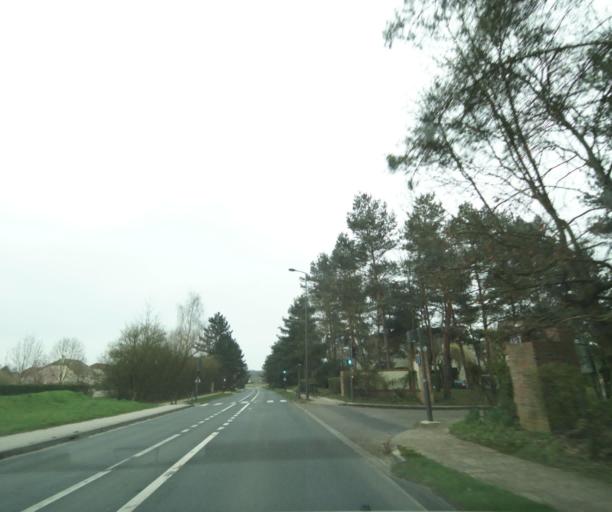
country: FR
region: Ile-de-France
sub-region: Departement du Val-d'Oise
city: Courdimanche
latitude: 49.0417
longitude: 2.0134
